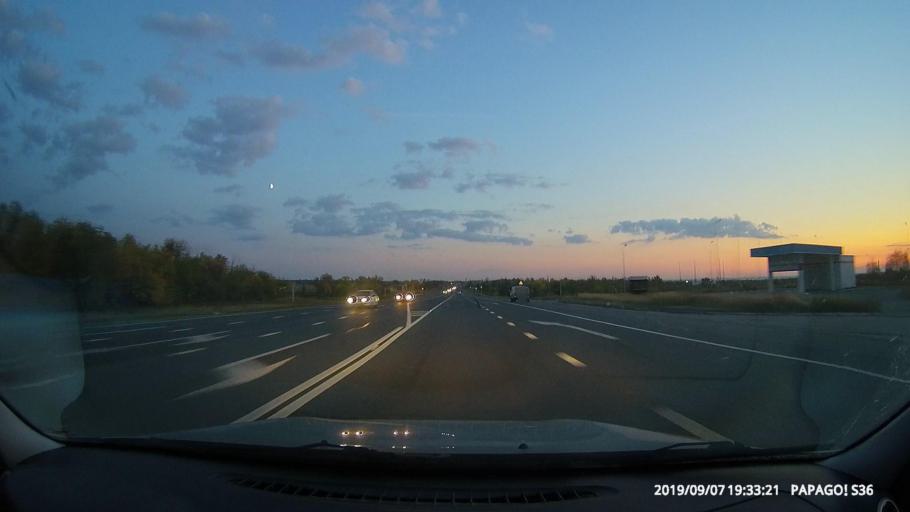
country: RU
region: Samara
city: Chapayevsk
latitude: 52.9959
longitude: 49.7747
